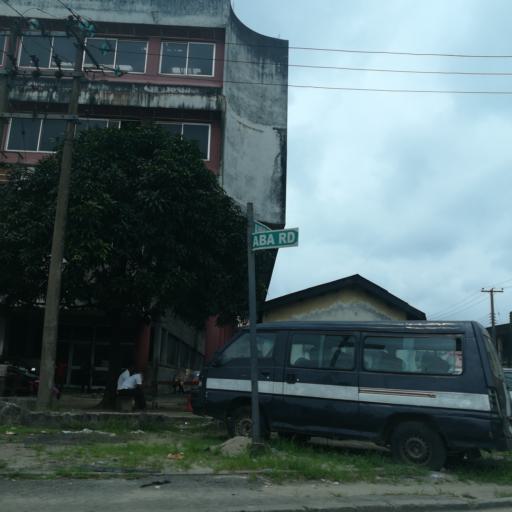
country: NG
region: Rivers
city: Port Harcourt
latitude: 4.7949
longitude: 7.0030
